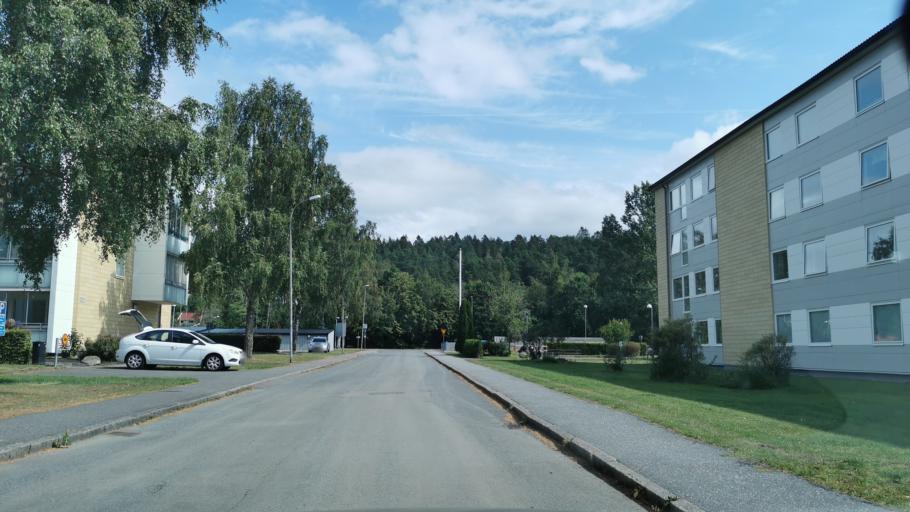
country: SE
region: Vaestra Goetaland
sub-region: Molndal
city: Moelndal
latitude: 57.6637
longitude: 11.9918
